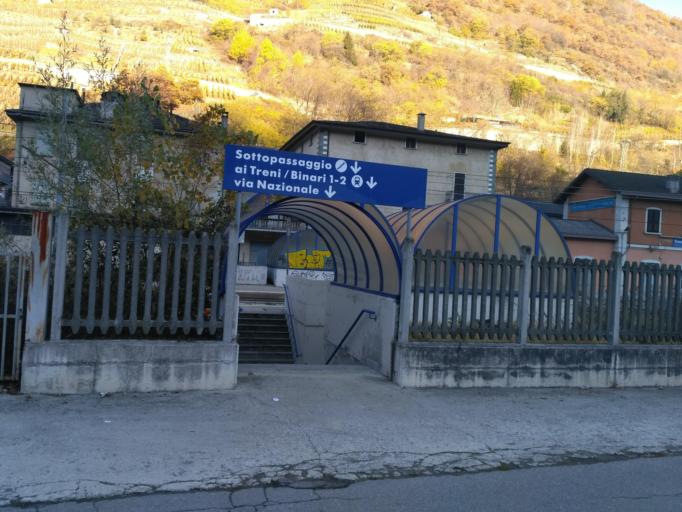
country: IT
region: Lombardy
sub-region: Provincia di Sondrio
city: Teglio
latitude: 46.1617
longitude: 10.0835
